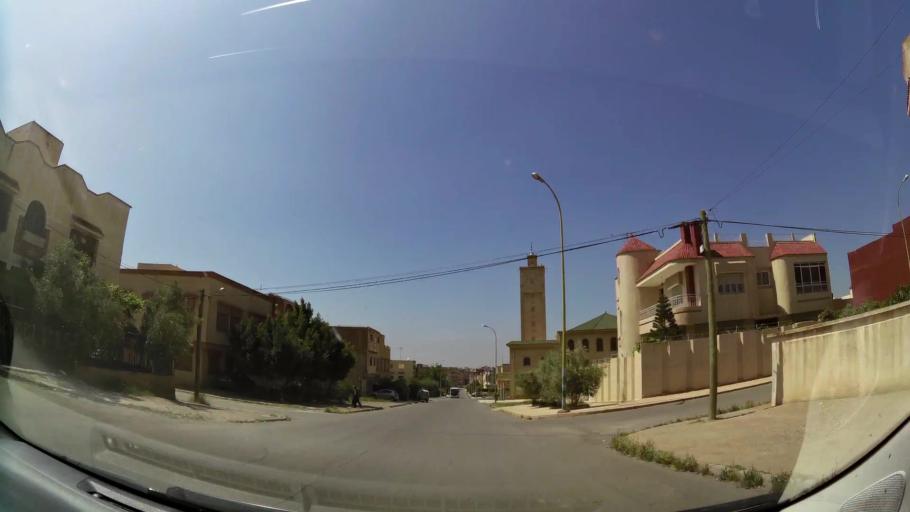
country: MA
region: Oriental
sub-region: Oujda-Angad
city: Oujda
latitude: 34.6915
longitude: -1.8805
